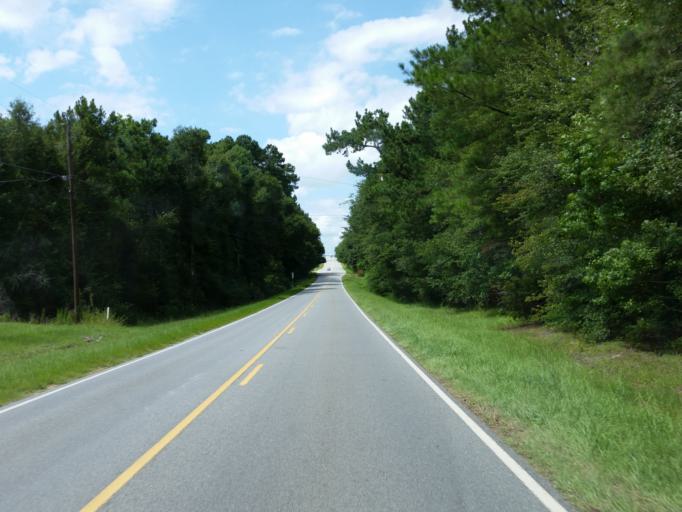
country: US
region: Georgia
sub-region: Tift County
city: Unionville
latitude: 31.4086
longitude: -83.5177
